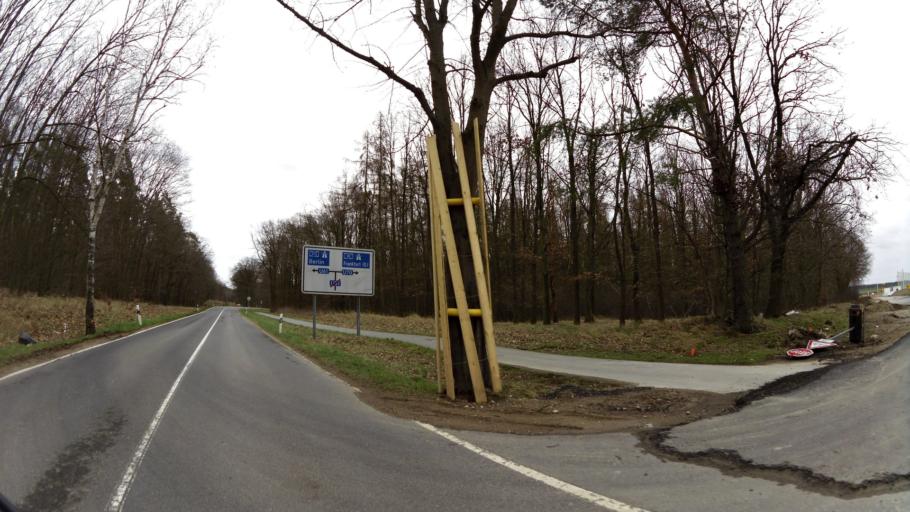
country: DE
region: Brandenburg
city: Schulzendorf
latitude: 52.3426
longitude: 13.5605
